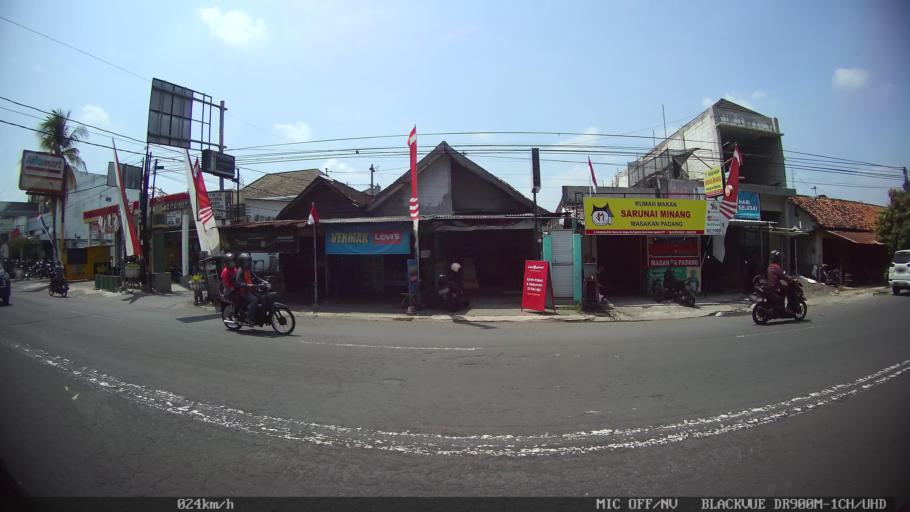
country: ID
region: Daerah Istimewa Yogyakarta
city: Yogyakarta
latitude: -7.8199
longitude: 110.4010
